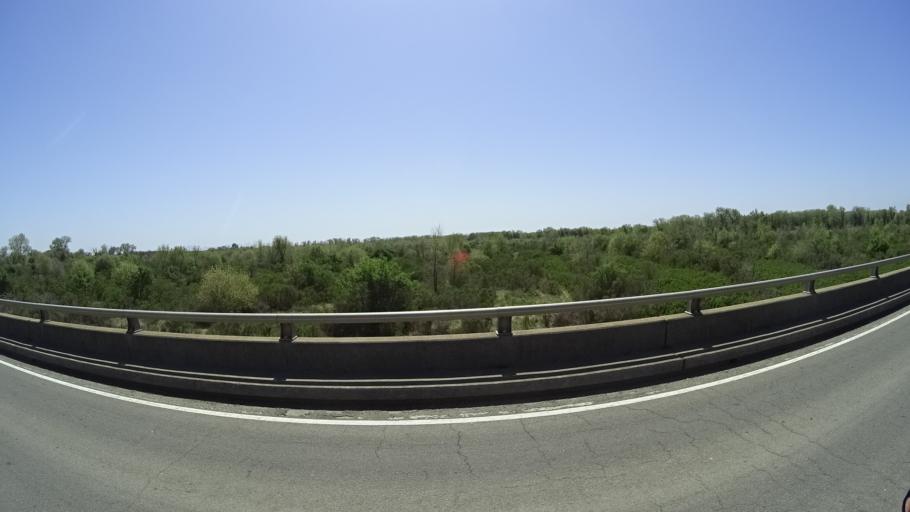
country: US
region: California
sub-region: Glenn County
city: Willows
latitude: 39.4570
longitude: -122.0023
